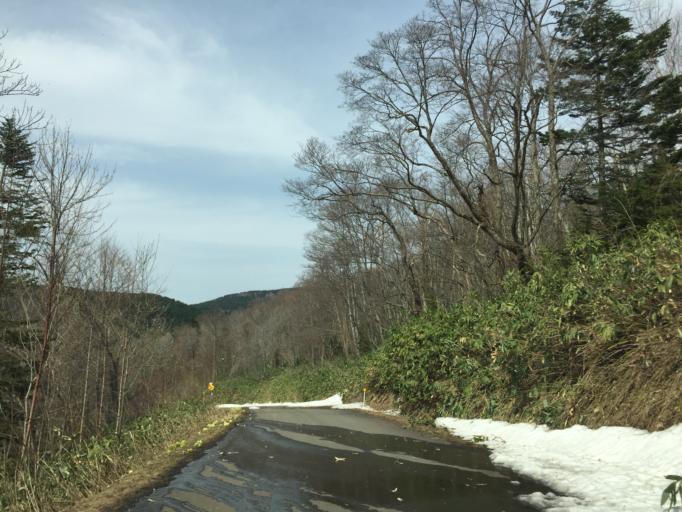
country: JP
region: Hokkaido
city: Akabira
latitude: 43.6009
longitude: 142.0646
